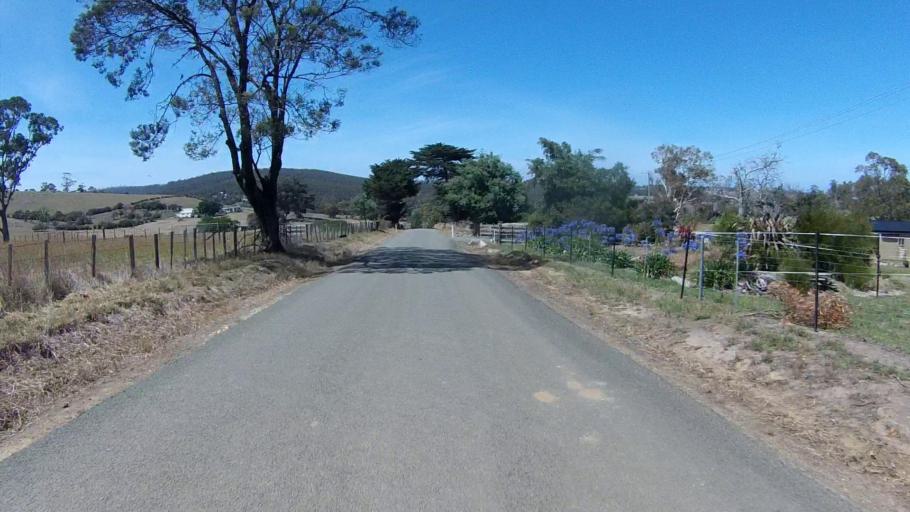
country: AU
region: Tasmania
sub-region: Sorell
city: Sorell
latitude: -42.7943
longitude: 147.6398
